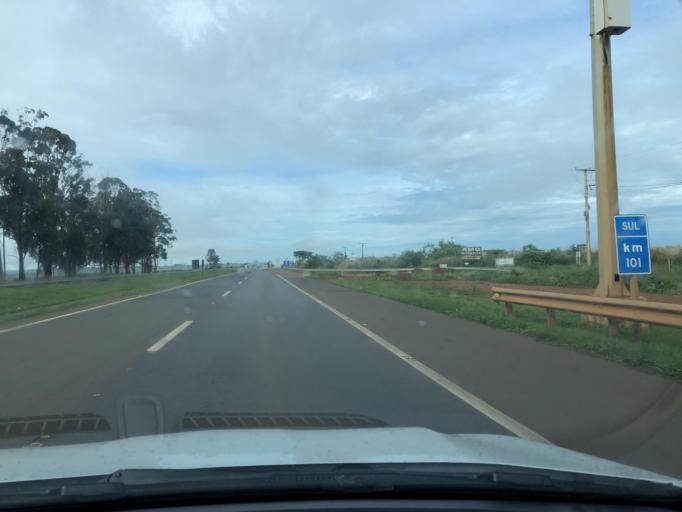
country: BR
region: Goias
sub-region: Cristalina
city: Cristalina
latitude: -16.7876
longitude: -47.6378
